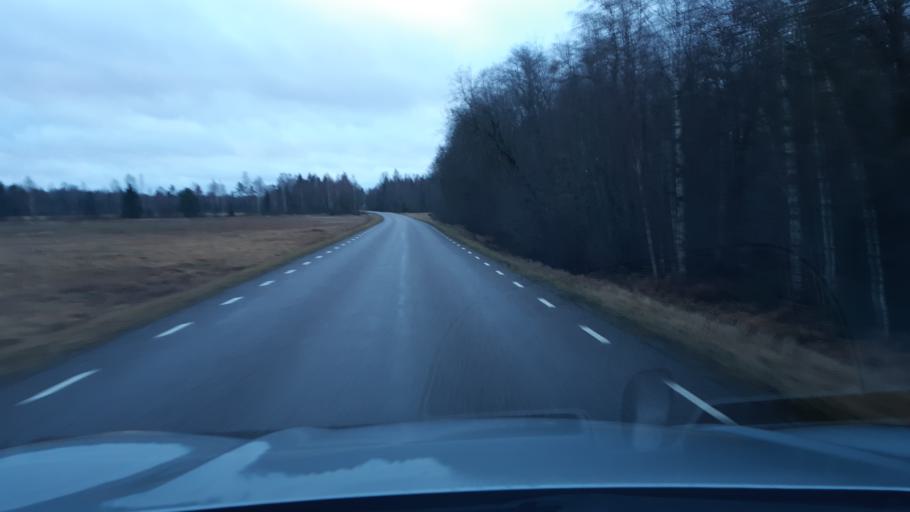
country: EE
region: Raplamaa
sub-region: Kohila vald
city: Kohila
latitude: 59.0886
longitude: 24.6742
